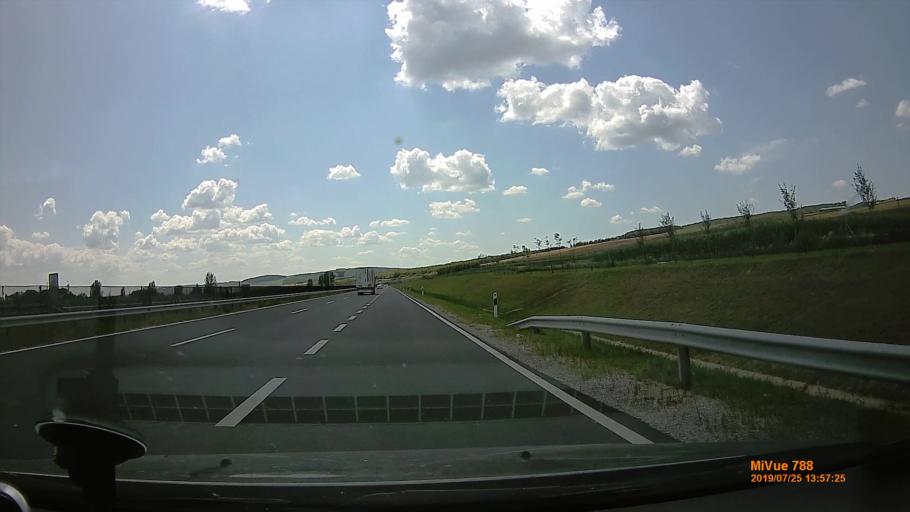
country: HU
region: Borsod-Abauj-Zemplen
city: Gonc
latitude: 48.5252
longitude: 21.2477
